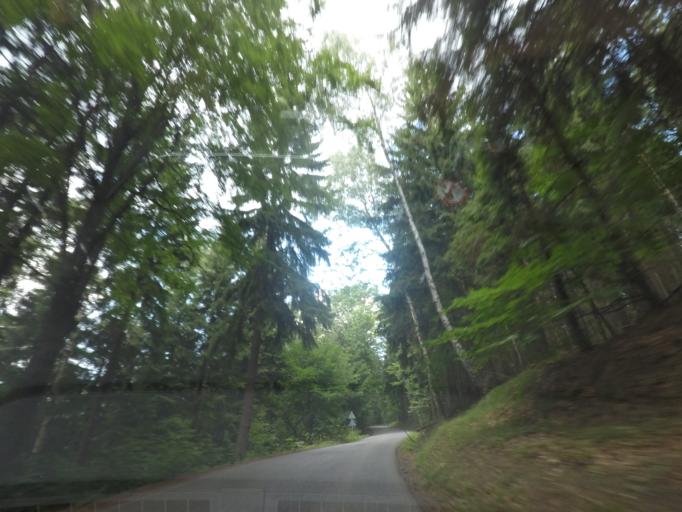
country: CZ
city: Radvanice
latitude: 50.6042
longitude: 16.0549
